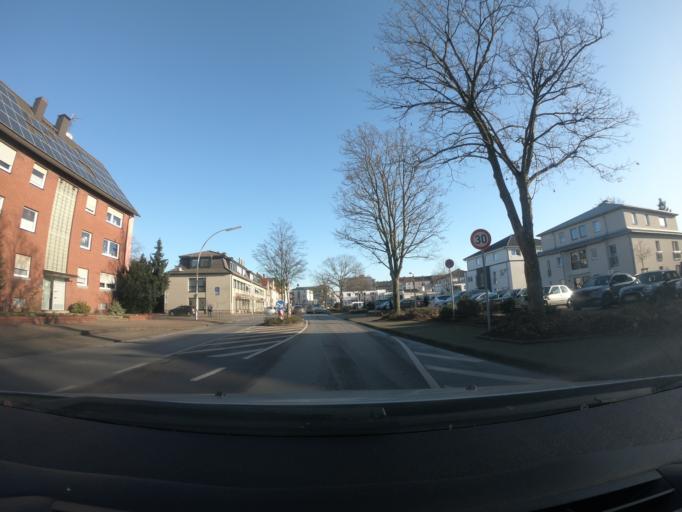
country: DE
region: North Rhine-Westphalia
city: Datteln
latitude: 51.6516
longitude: 7.3356
